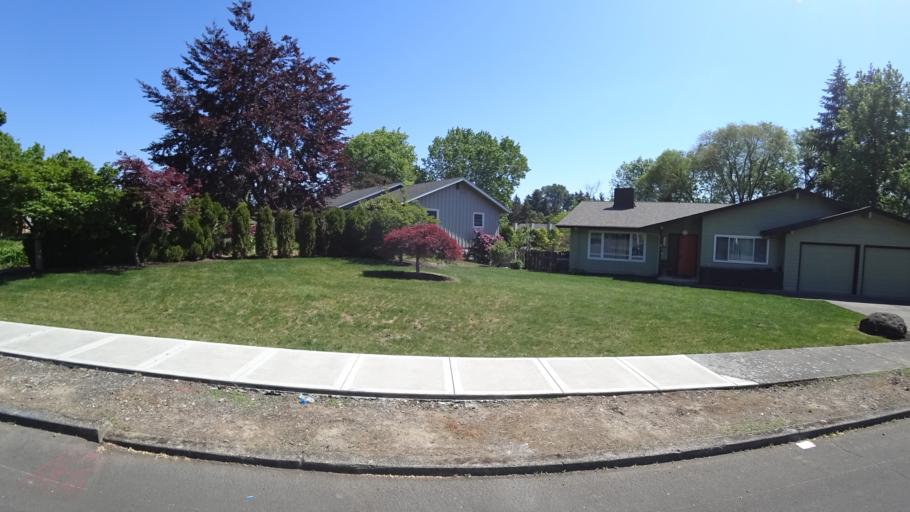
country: US
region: Oregon
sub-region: Washington County
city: Rockcreek
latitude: 45.5468
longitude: -122.8743
